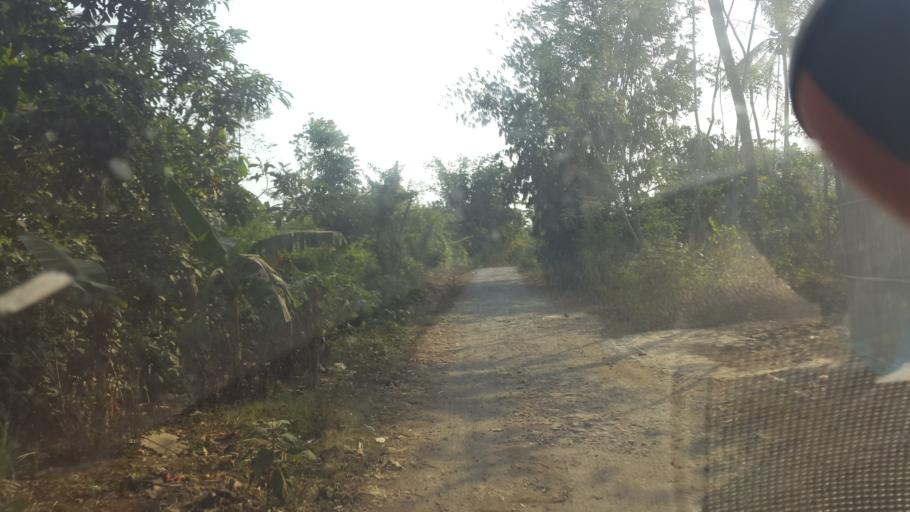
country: ID
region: West Java
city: Citanglar
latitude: -7.3208
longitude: 106.5824
